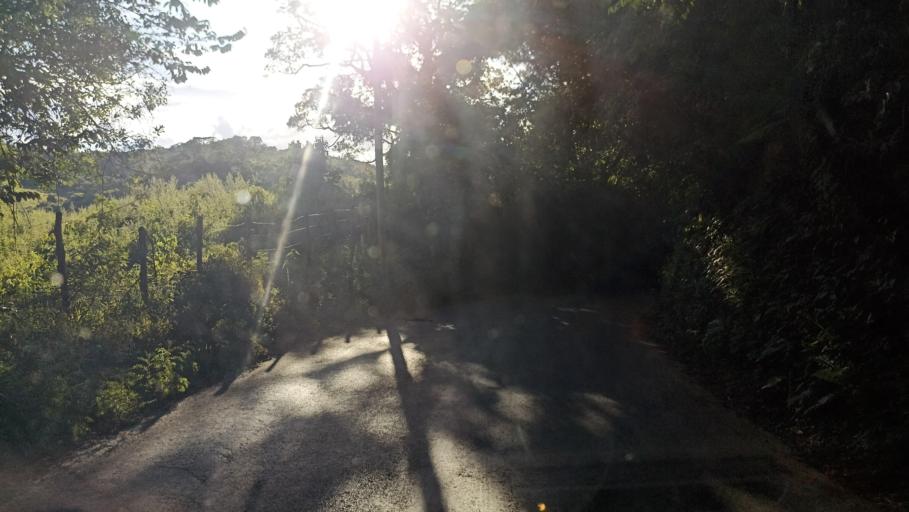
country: BR
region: Minas Gerais
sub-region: Ouro Preto
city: Ouro Preto
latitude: -20.3136
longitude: -43.5962
